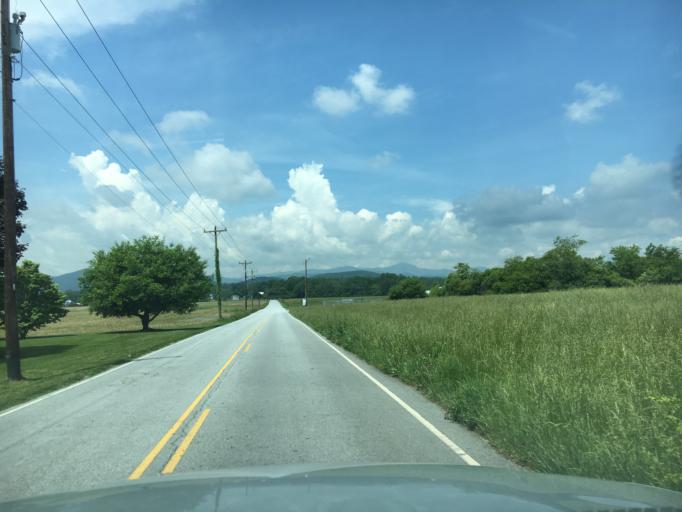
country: US
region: North Carolina
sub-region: Henderson County
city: Mills River
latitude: 35.3774
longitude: -82.5510
